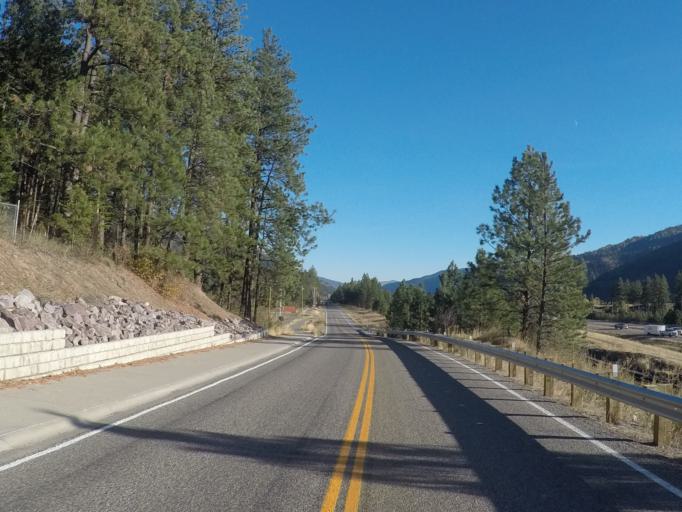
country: US
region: Montana
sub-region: Missoula County
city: Bonner-West Riverside
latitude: 46.8460
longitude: -113.8444
